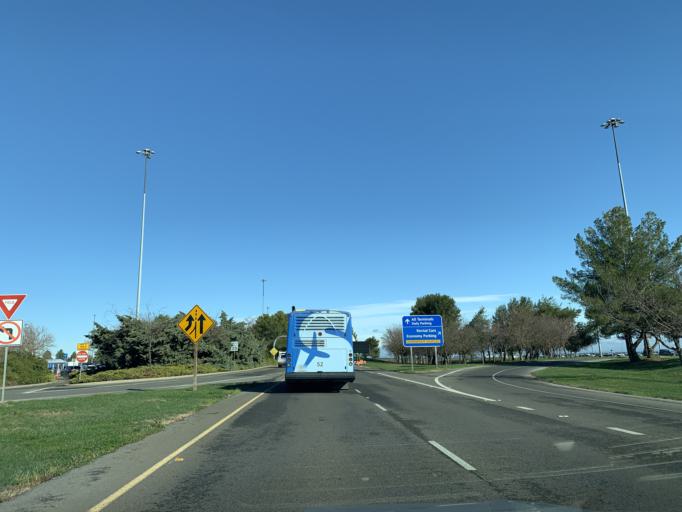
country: US
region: California
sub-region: Yolo County
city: West Sacramento
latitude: 38.6856
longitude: -121.5891
